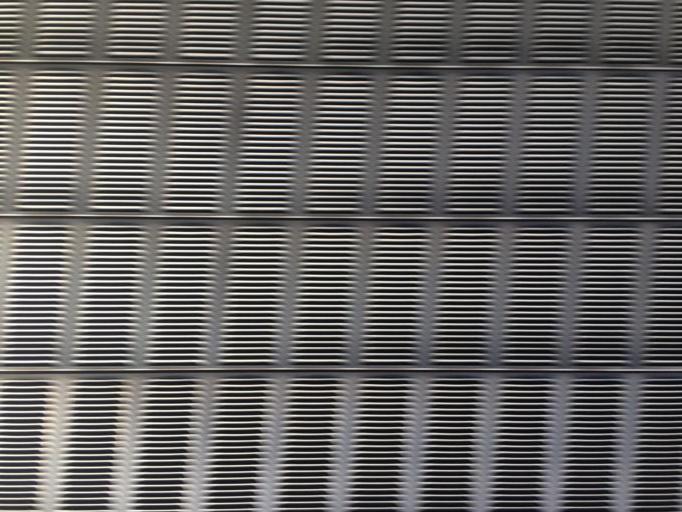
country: JP
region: Hyogo
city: Kobe
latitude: 34.7060
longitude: 135.2342
